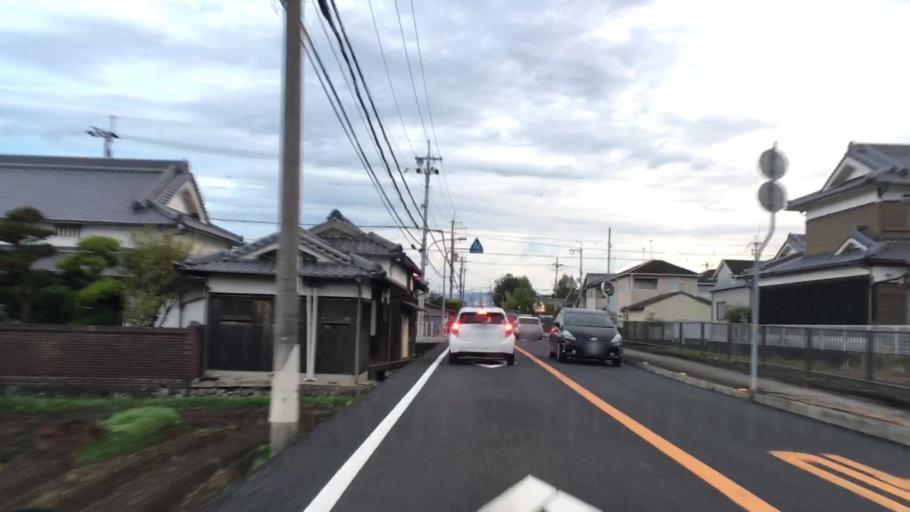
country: JP
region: Hyogo
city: Himeji
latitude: 34.9028
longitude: 134.7358
